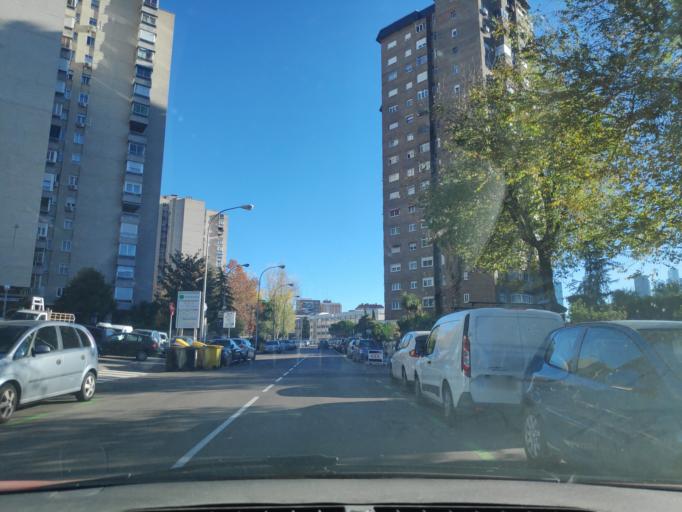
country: ES
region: Madrid
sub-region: Provincia de Madrid
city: Tetuan de las Victorias
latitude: 40.4826
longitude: -3.7105
